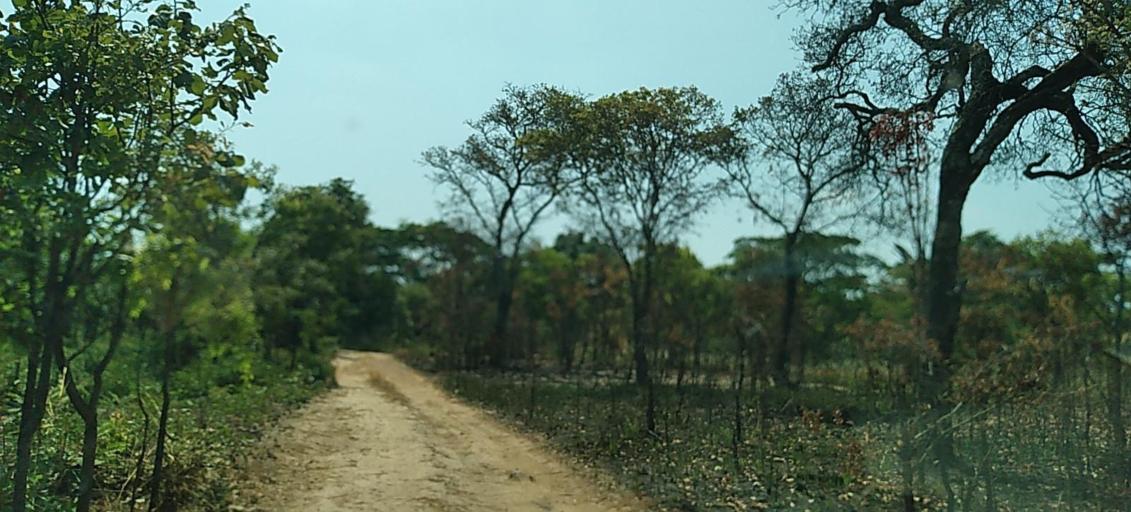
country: ZM
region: North-Western
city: Solwezi
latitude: -12.0985
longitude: 26.2797
